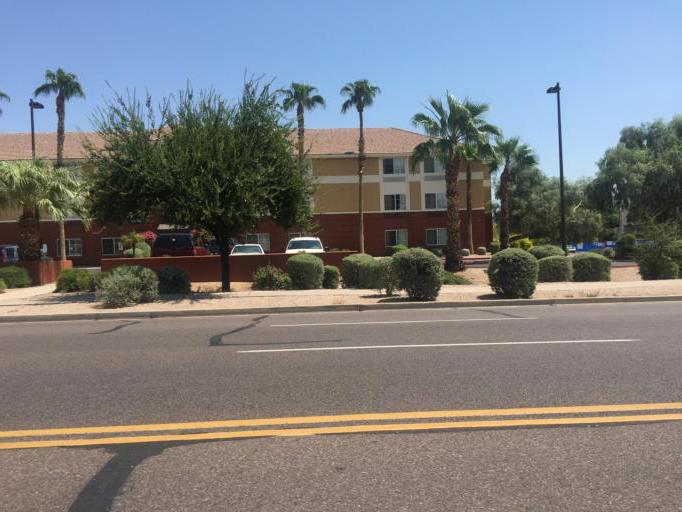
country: US
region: Arizona
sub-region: Maricopa County
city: Phoenix
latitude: 33.5133
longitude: -112.0475
